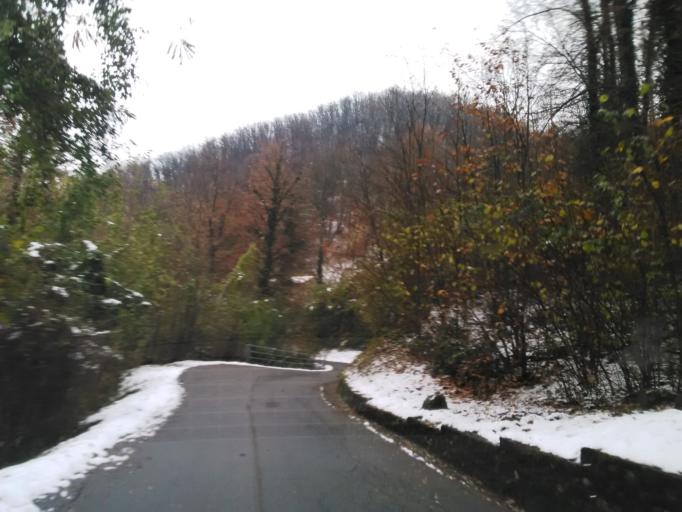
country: IT
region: Piedmont
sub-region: Provincia di Vercelli
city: Varallo
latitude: 45.8014
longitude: 8.2565
